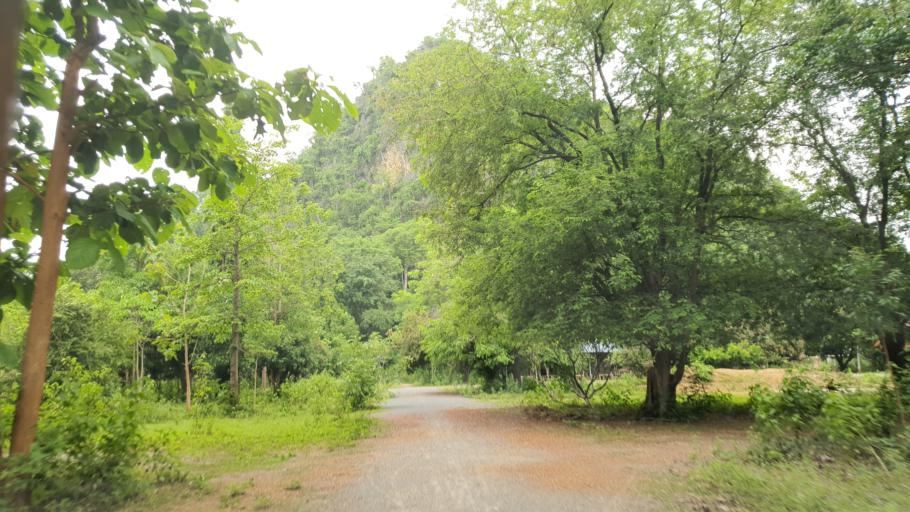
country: TH
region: Sukhothai
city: Thung Saliam
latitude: 17.2387
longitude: 99.5433
